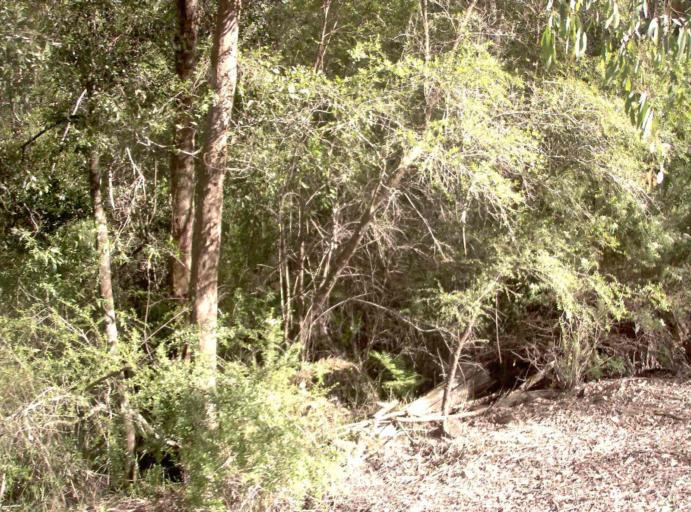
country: AU
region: Victoria
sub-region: East Gippsland
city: Lakes Entrance
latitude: -37.4760
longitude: 148.5568
